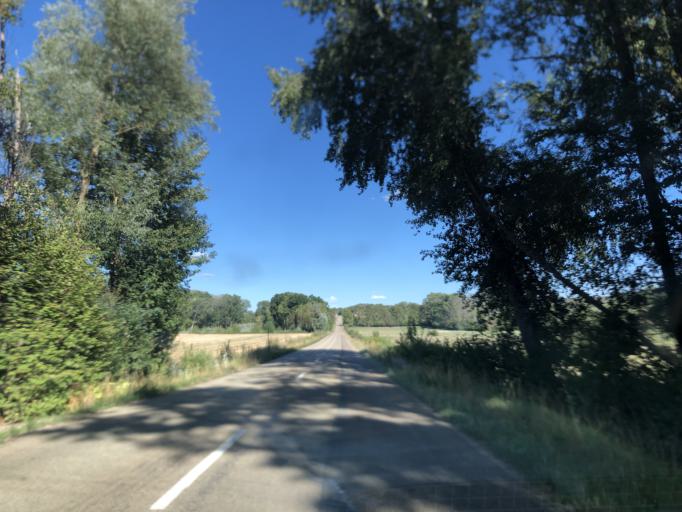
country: FR
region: Bourgogne
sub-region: Departement de l'Yonne
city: Seignelay
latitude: 47.8997
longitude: 3.5786
